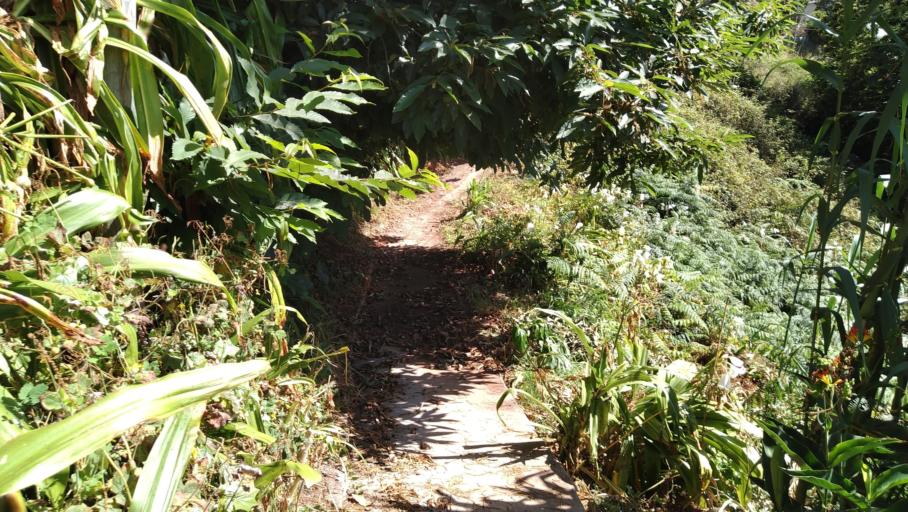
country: PT
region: Madeira
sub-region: Funchal
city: Nossa Senhora do Monte
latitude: 32.6818
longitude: -16.9412
